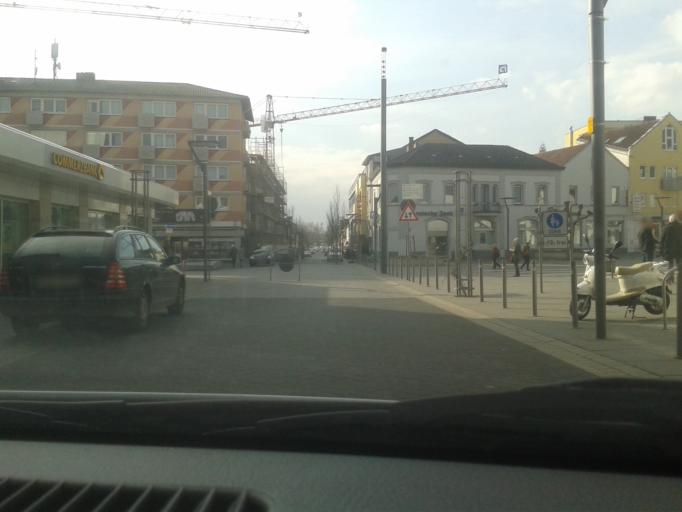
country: DE
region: Rheinland-Pfalz
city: Ingelheim am Rhein
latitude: 49.9747
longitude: 8.0550
